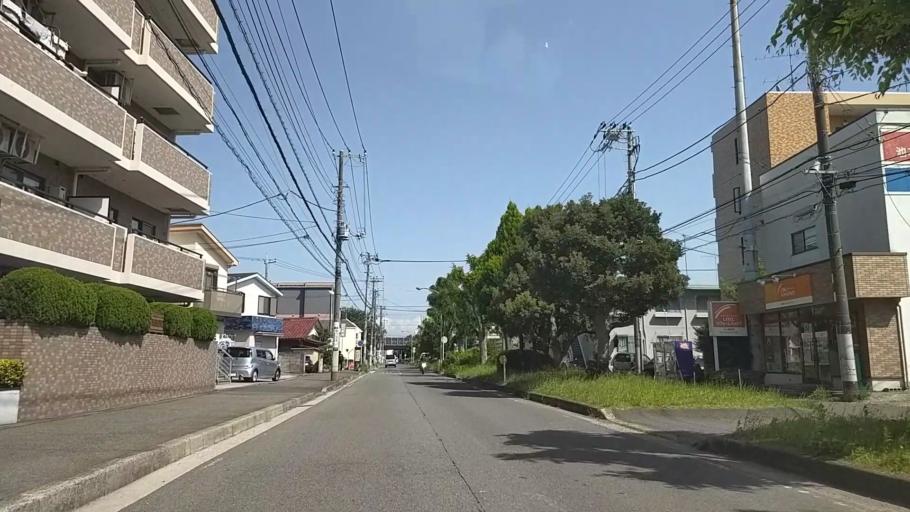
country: JP
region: Kanagawa
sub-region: Kawasaki-shi
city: Kawasaki
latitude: 35.5423
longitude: 139.6447
